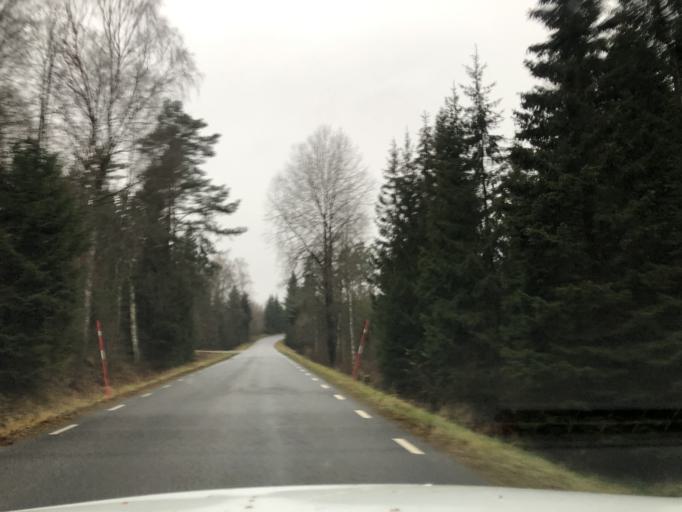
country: SE
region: Vaestra Goetaland
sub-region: Ulricehamns Kommun
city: Ulricehamn
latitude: 57.8335
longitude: 13.3929
